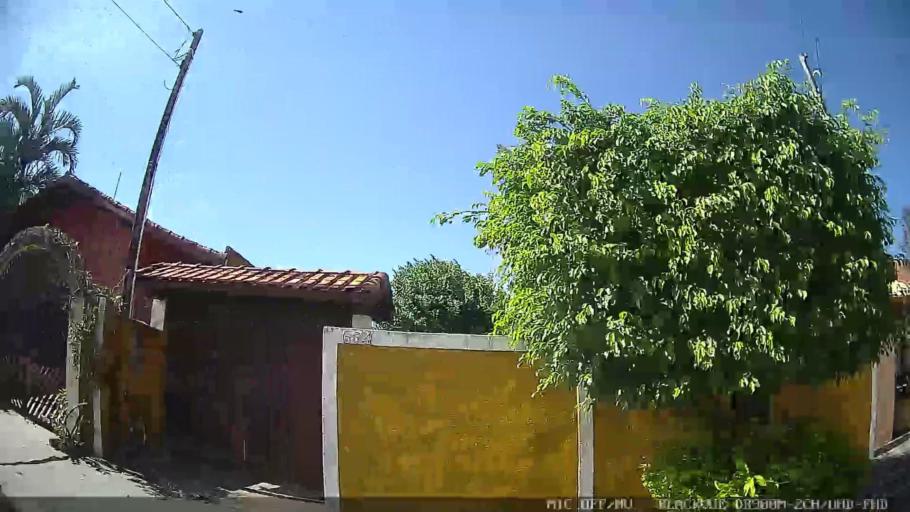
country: BR
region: Sao Paulo
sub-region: Peruibe
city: Peruibe
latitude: -24.2960
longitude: -46.9746
